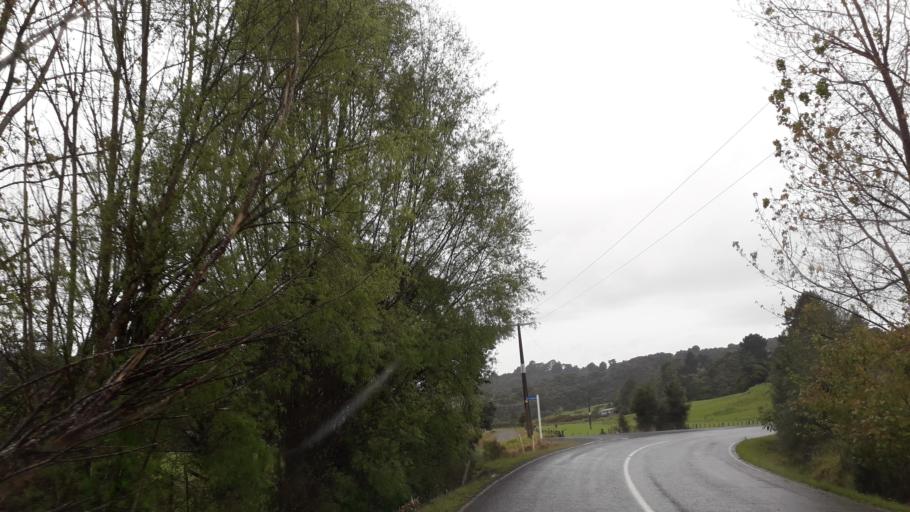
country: NZ
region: Northland
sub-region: Far North District
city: Kaitaia
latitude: -35.3601
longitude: 173.4817
